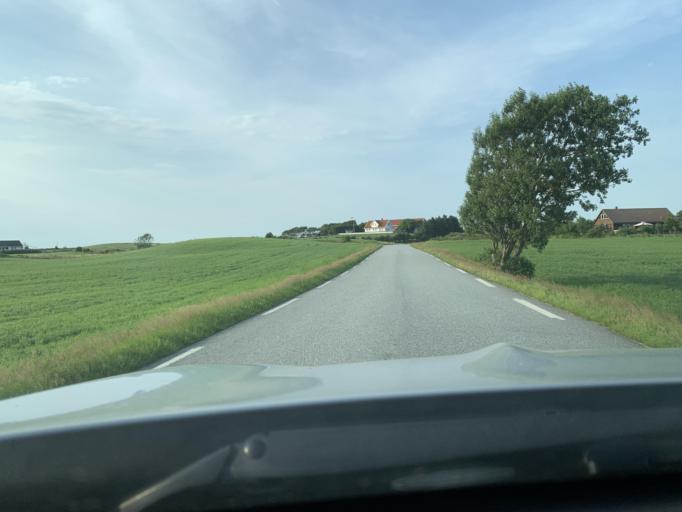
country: NO
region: Rogaland
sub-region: Time
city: Bryne
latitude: 58.7281
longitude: 5.5862
